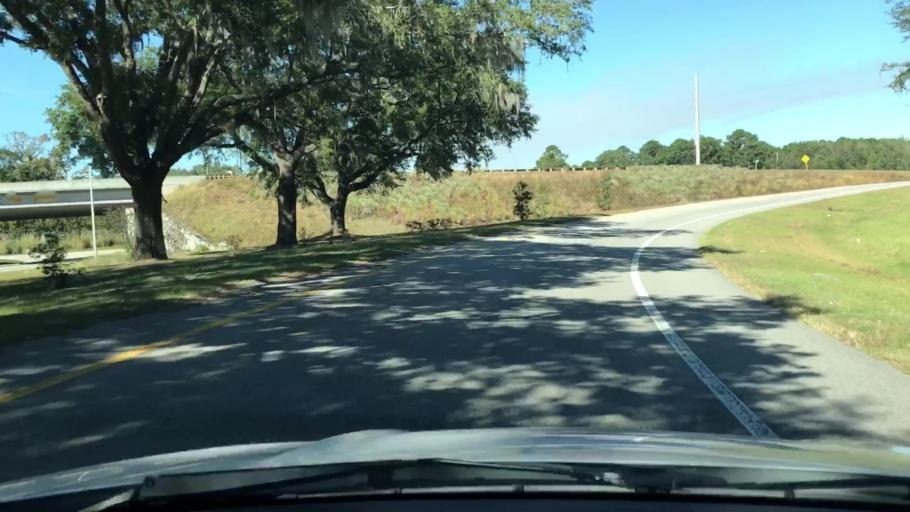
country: US
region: South Carolina
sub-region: Hampton County
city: Yemassee
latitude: 32.6010
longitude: -80.7589
